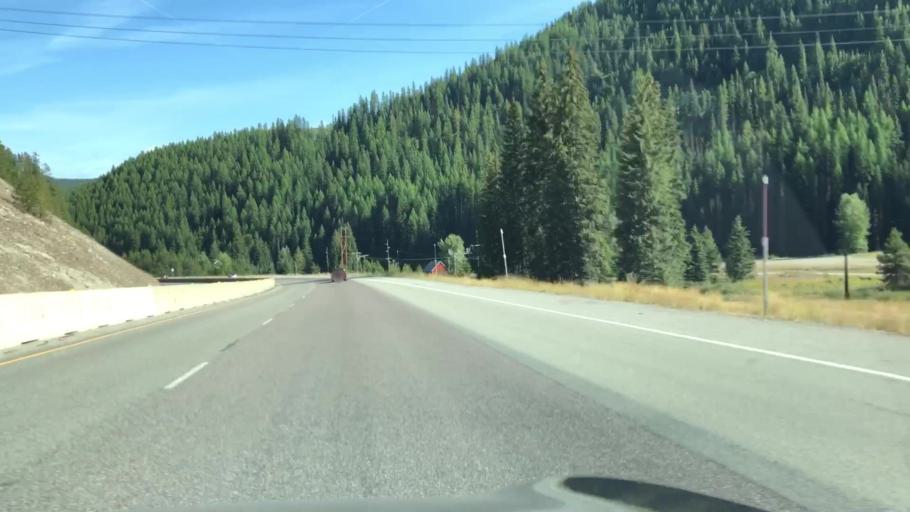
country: US
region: Montana
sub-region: Sanders County
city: Thompson Falls
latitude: 47.4202
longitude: -115.6032
